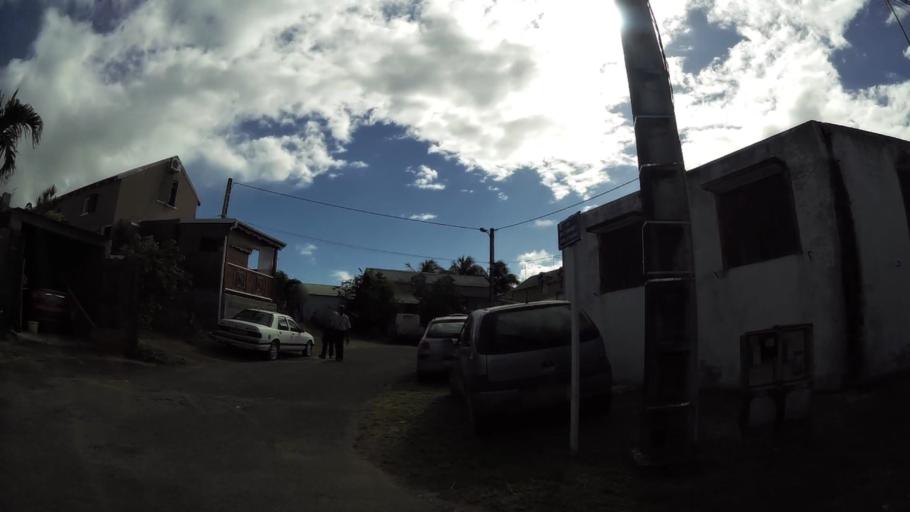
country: GP
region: Guadeloupe
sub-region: Guadeloupe
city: Port-Louis
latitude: 16.4162
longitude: -61.5256
